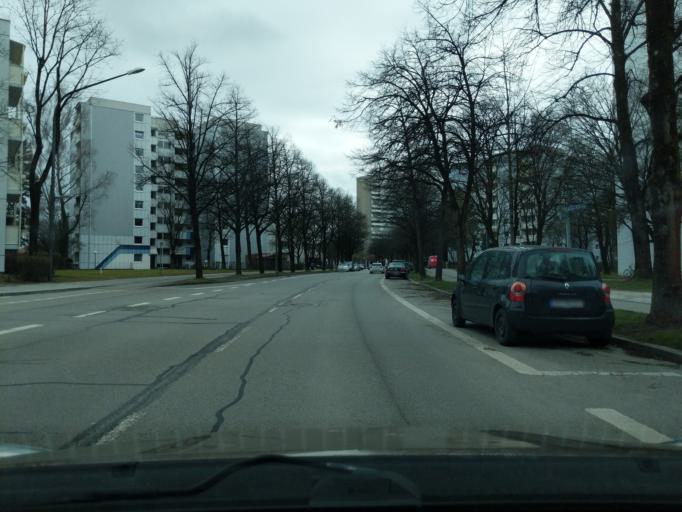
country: DE
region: Bavaria
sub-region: Upper Bavaria
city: Bogenhausen
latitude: 48.1607
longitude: 11.6442
